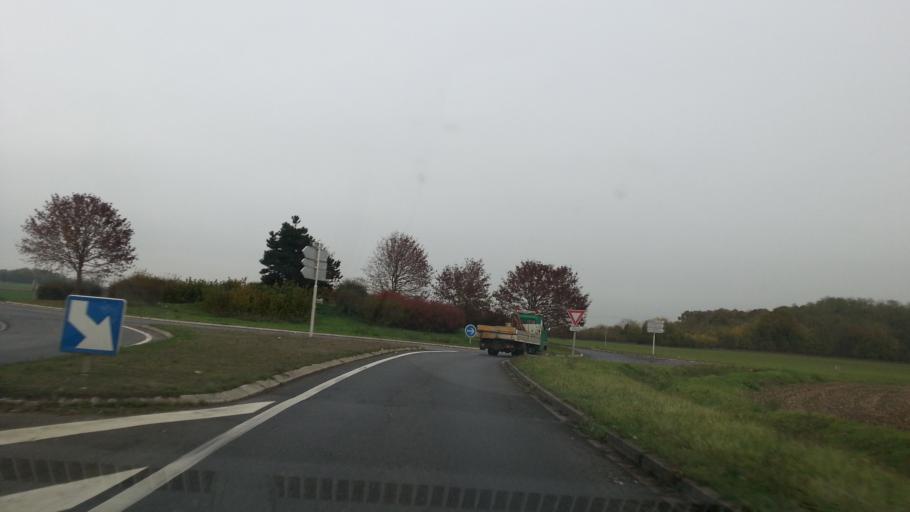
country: FR
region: Picardie
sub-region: Departement de l'Oise
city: Boran-sur-Oise
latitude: 49.1756
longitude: 2.3518
